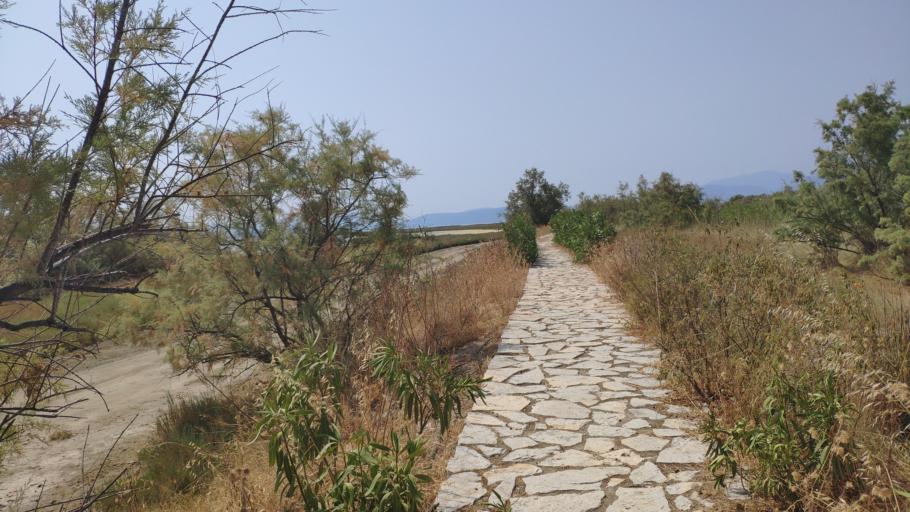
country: GR
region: West Greece
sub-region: Nomos Aitolias kai Akarnanias
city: Menidi
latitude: 39.0366
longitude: 21.0745
